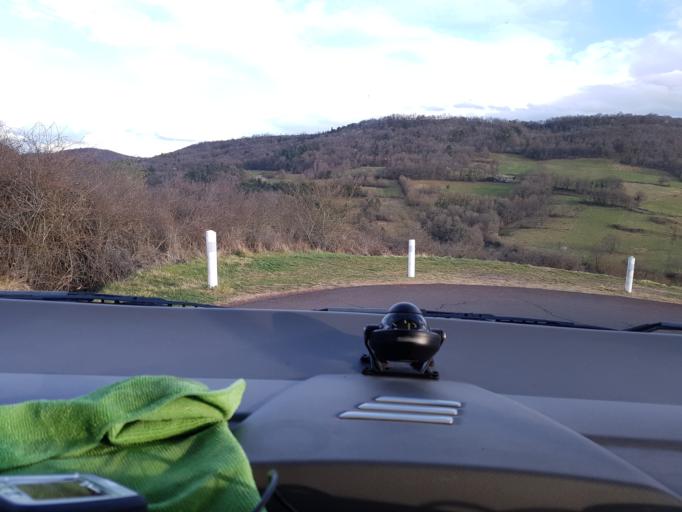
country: FR
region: Auvergne
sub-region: Departement du Cantal
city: Massiac
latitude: 45.2887
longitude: 3.1955
